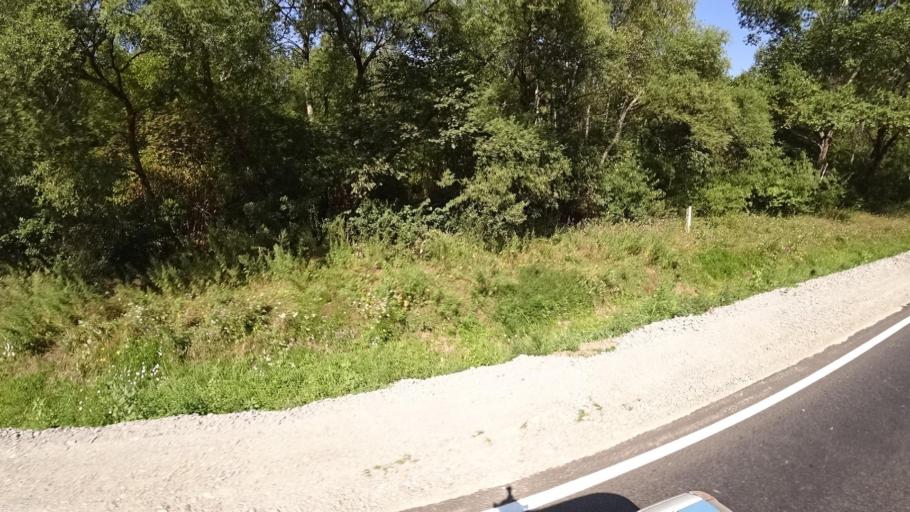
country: RU
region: Khabarovsk Krai
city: Khor
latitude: 47.9768
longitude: 135.0741
